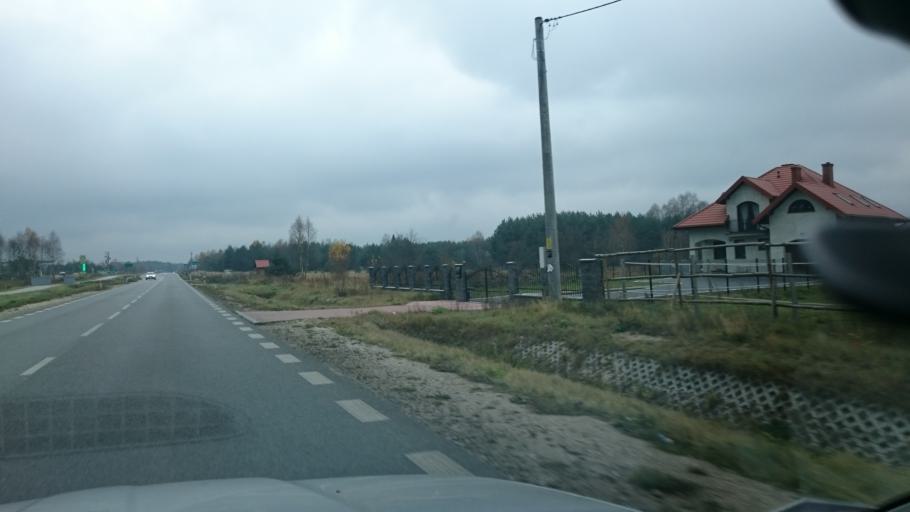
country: PL
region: Swietokrzyskie
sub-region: Powiat konecki
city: Konskie
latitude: 51.1370
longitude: 20.3632
